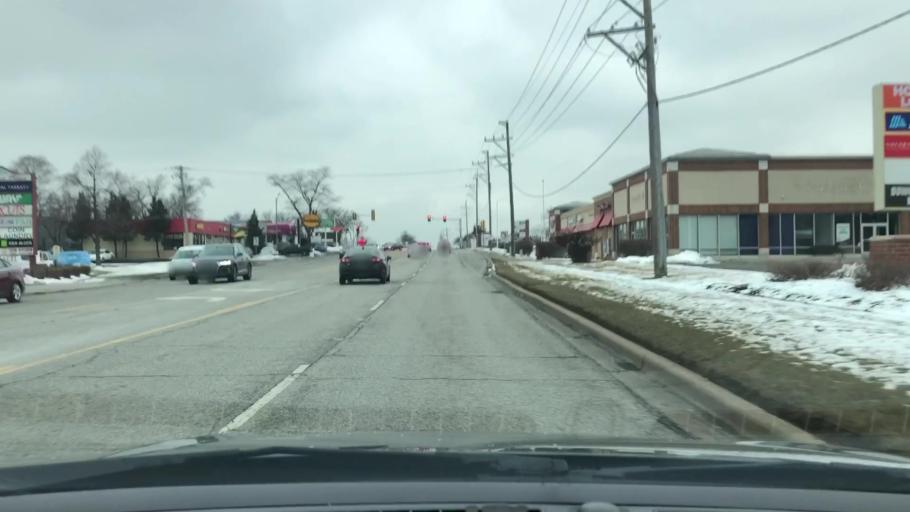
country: US
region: Illinois
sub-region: DuPage County
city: Westmont
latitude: 41.8098
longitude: -87.9862
